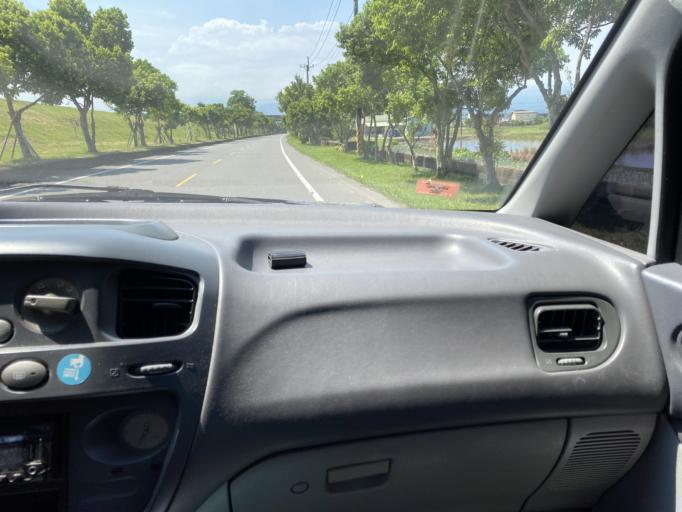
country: TW
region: Taiwan
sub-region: Yilan
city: Yilan
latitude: 24.7191
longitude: 121.7918
